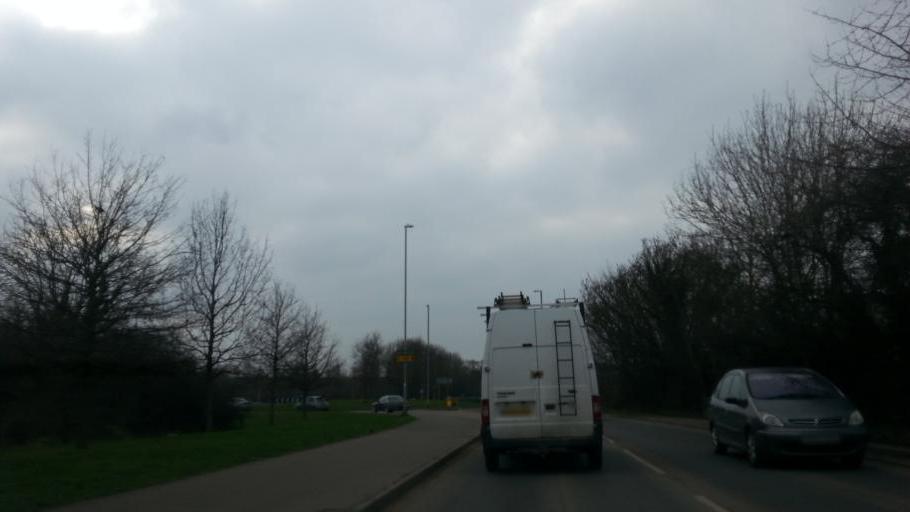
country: GB
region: England
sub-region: Northamptonshire
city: Corby
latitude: 52.4812
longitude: -0.7035
